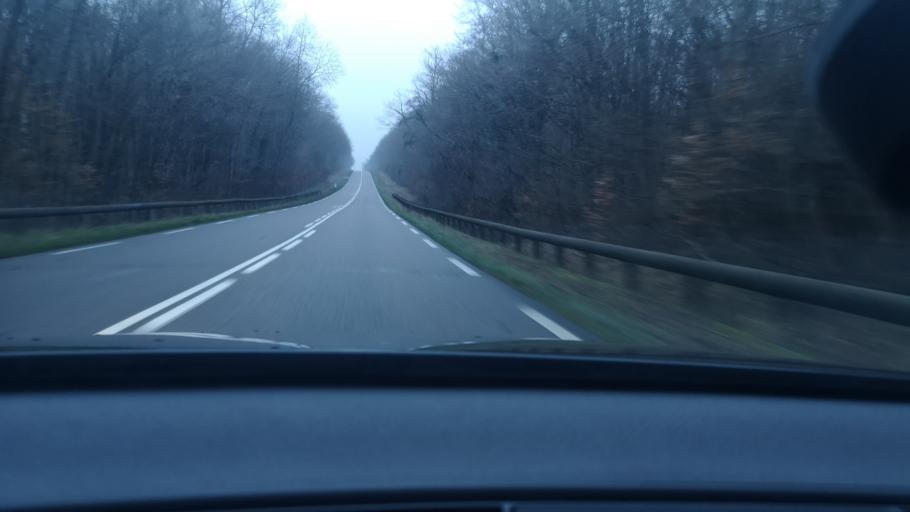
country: FR
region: Bourgogne
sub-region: Departement de la Cote-d'Or
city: Aiserey
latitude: 47.1009
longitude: 5.1031
